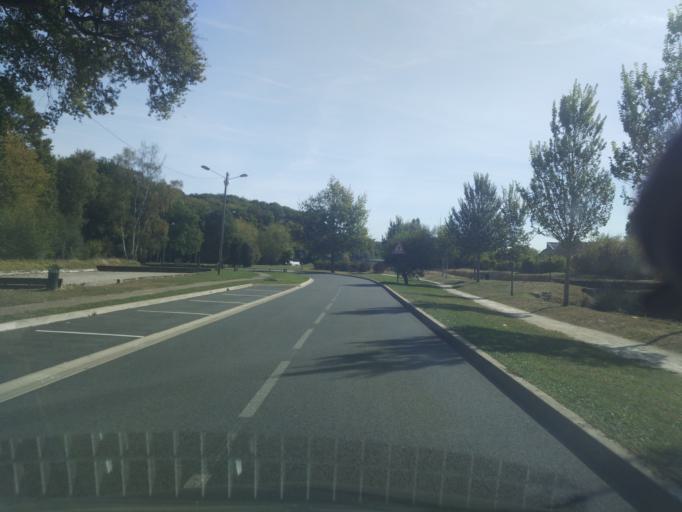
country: FR
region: Ile-de-France
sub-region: Departement de l'Essonne
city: Limours
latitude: 48.6456
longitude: 2.0864
